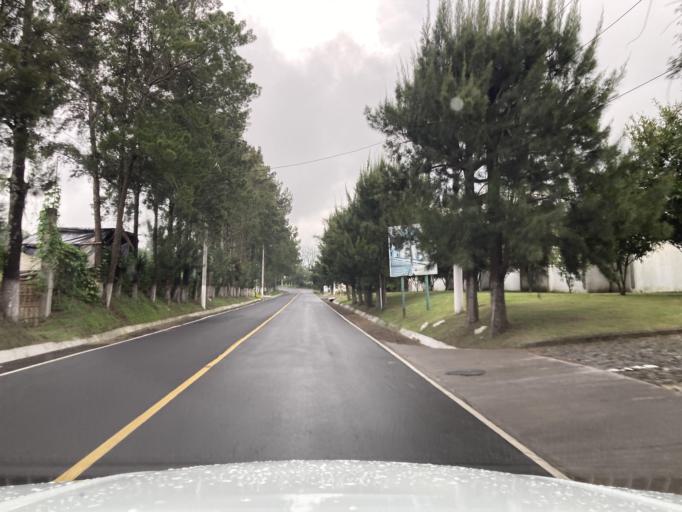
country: GT
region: Sacatepequez
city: San Miguel Duenas
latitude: 14.5184
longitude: -90.7869
